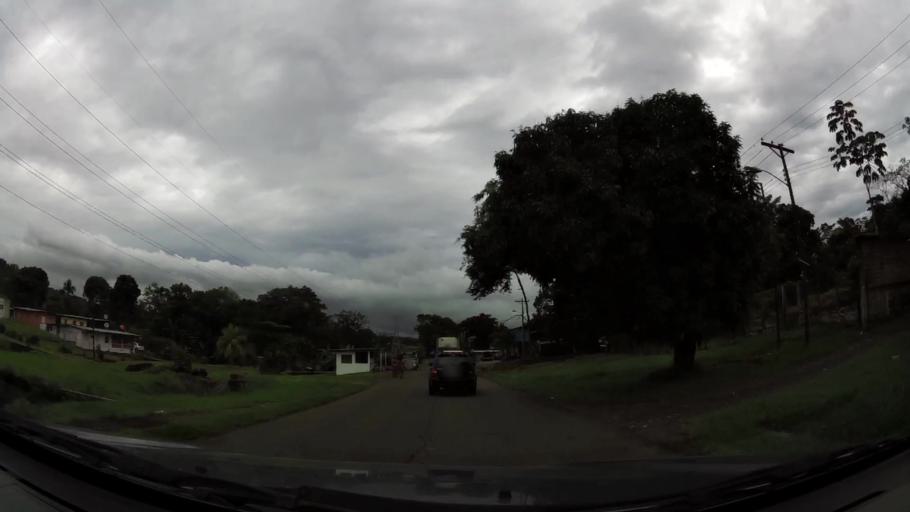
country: PA
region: Panama
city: Chilibre
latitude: 9.1412
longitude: -79.6157
